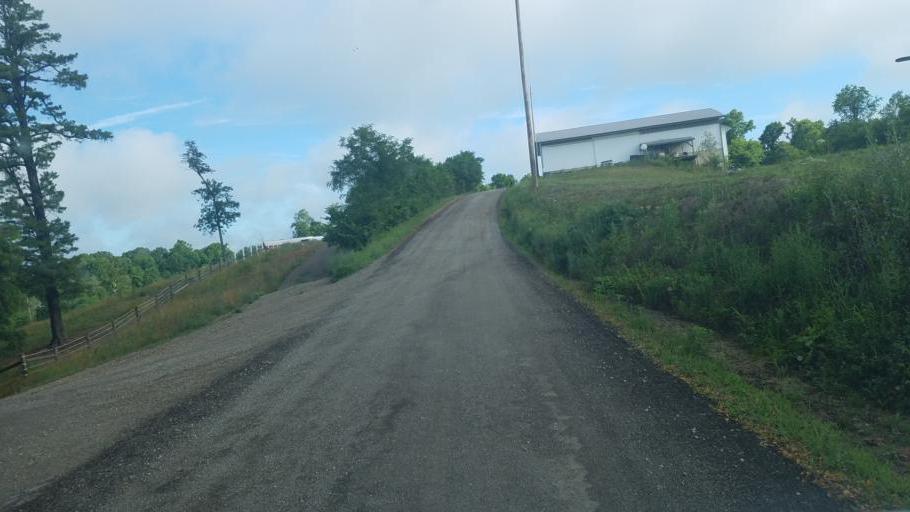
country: US
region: Ohio
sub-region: Gallia County
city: Gallipolis
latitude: 38.7359
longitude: -82.3436
